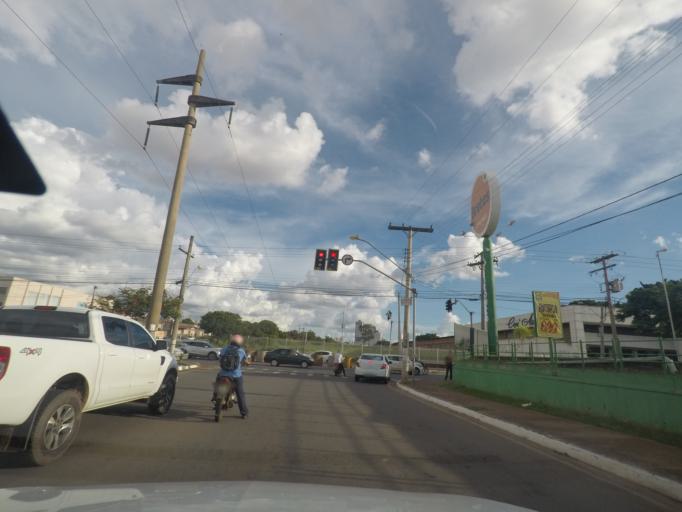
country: BR
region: Goias
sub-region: Goiania
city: Goiania
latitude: -16.6847
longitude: -49.2924
